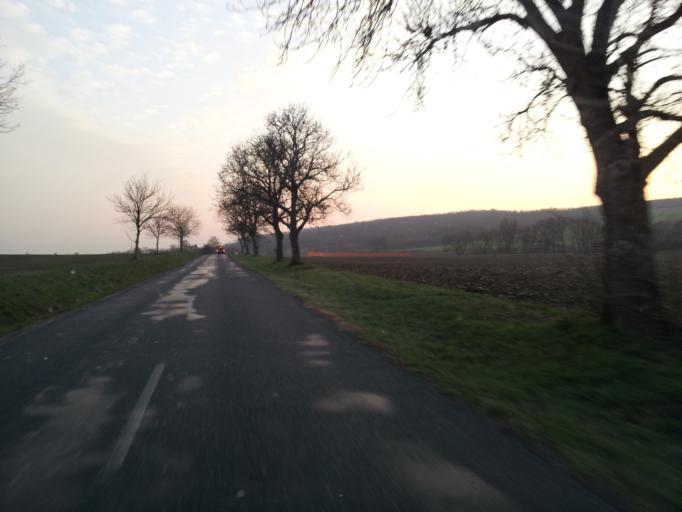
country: HU
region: Zala
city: Cserszegtomaj
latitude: 46.8334
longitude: 17.1955
